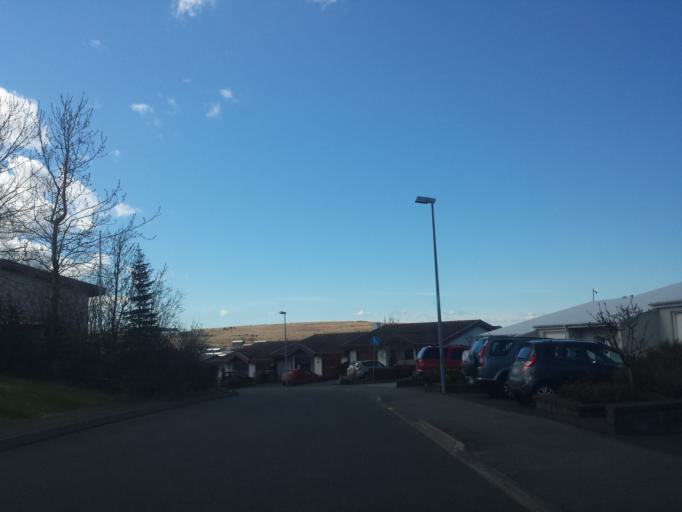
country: IS
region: Capital Region
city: Reykjavik
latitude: 64.1007
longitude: -21.8636
